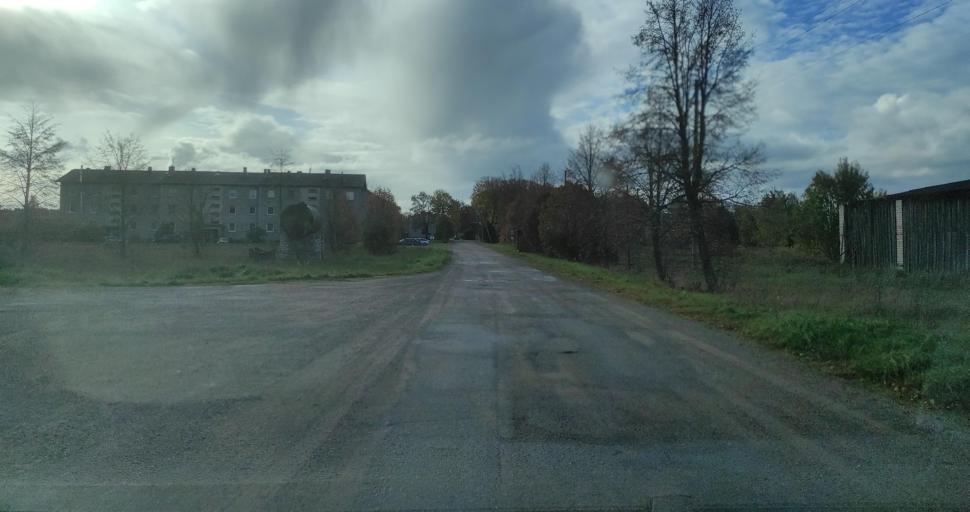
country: LV
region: Skrunda
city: Skrunda
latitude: 56.6847
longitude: 22.0478
